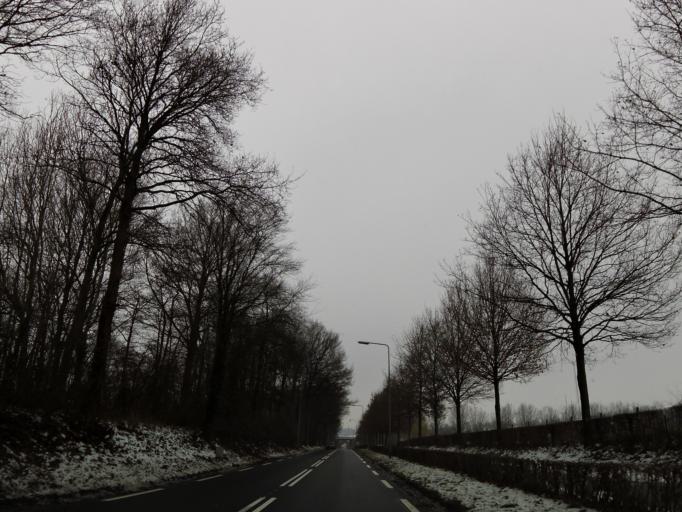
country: NL
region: Limburg
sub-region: Gemeente Simpelveld
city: Simpelveld
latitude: 50.8246
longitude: 5.9960
